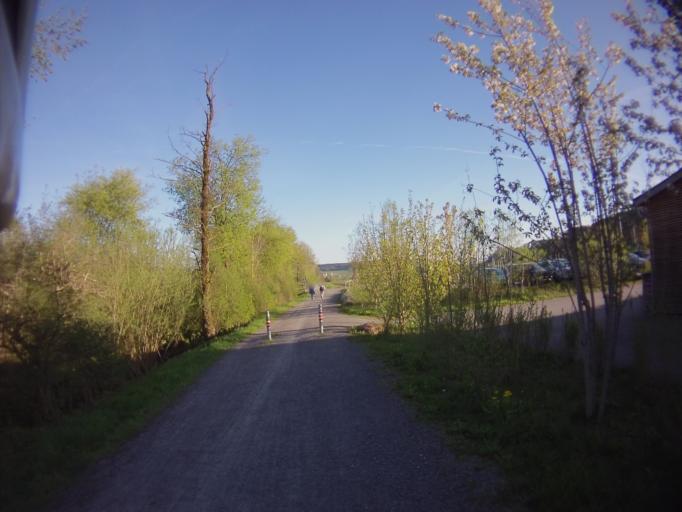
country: CH
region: Zurich
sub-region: Bezirk Affoltern
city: Wettswil / Wettswil (Dorf)
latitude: 47.3358
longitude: 8.4653
